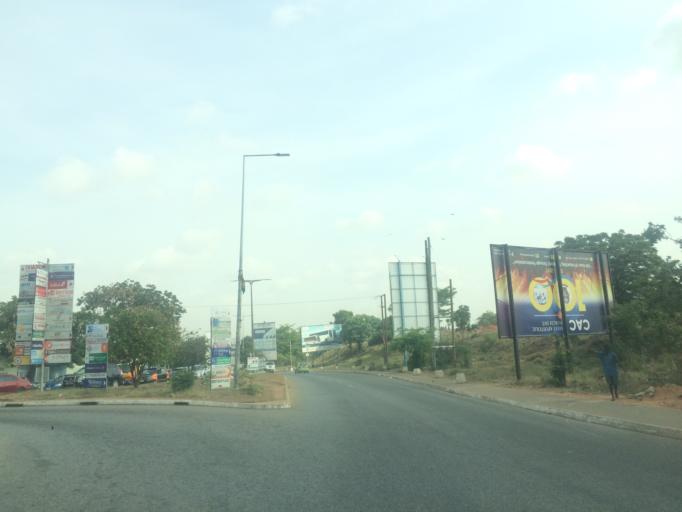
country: GH
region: Greater Accra
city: Accra
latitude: 5.5629
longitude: -0.2016
